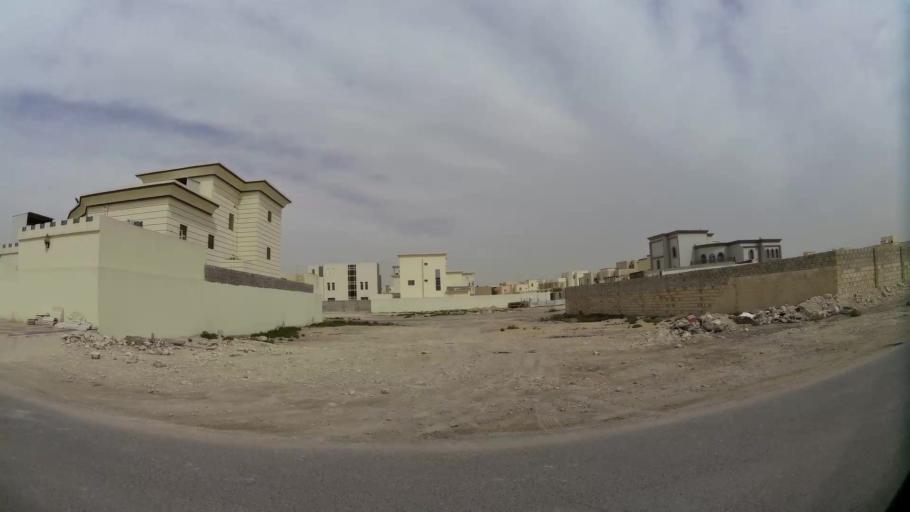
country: QA
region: Baladiyat ad Dawhah
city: Doha
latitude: 25.2151
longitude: 51.4810
